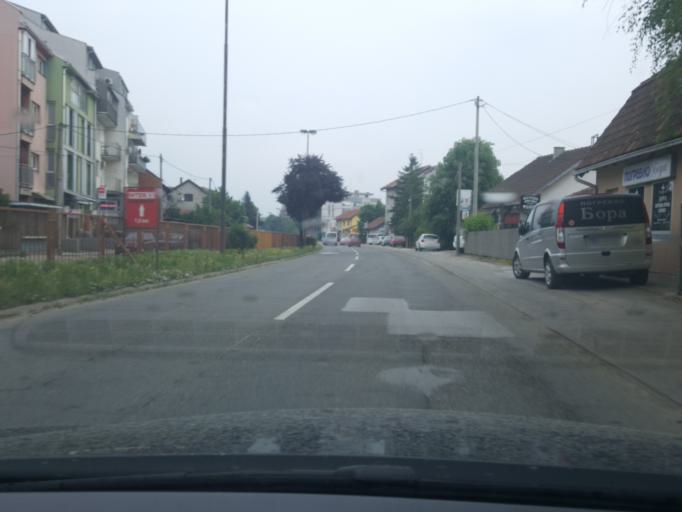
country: RS
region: Central Serbia
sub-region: Kolubarski Okrug
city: Valjevo
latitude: 44.2735
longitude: 19.8945
